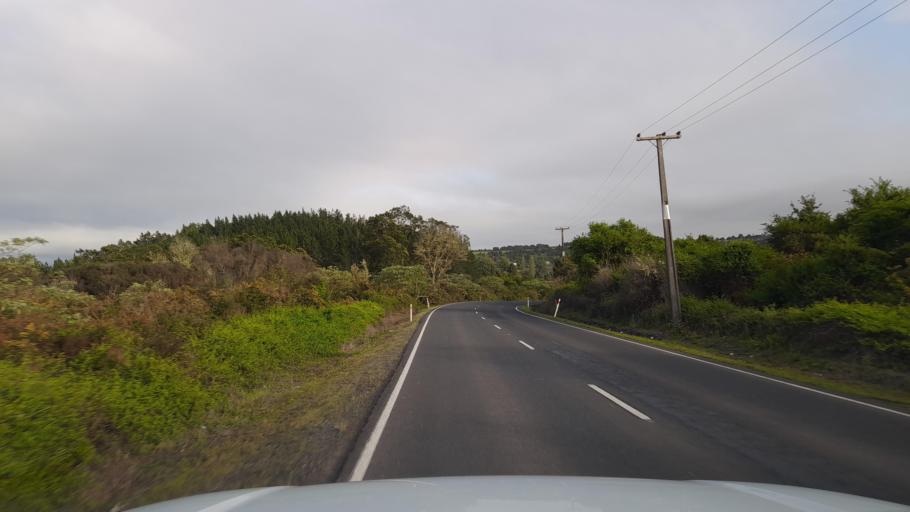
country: NZ
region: Northland
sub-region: Far North District
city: Waimate North
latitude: -35.4651
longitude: 173.8311
